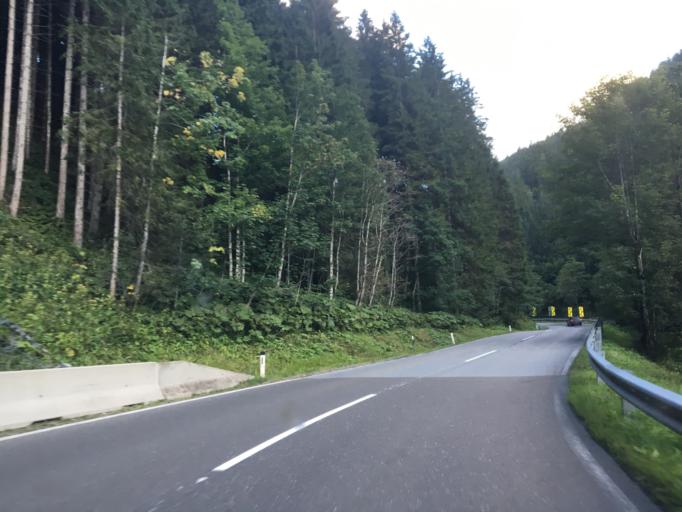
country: AT
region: Styria
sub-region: Politischer Bezirk Murtal
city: Hohentauern
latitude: 47.4522
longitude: 14.4983
